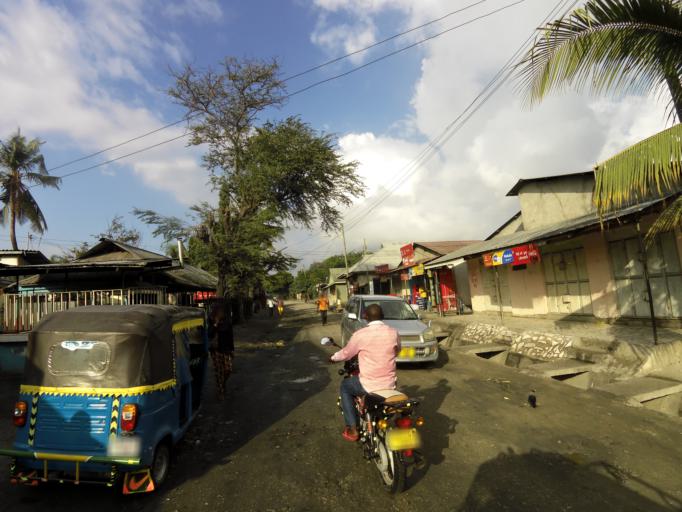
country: TZ
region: Dar es Salaam
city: Magomeni
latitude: -6.7898
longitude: 39.2308
